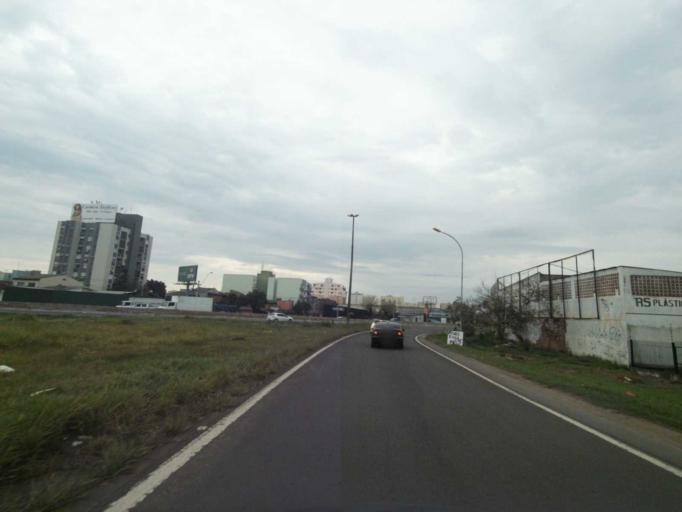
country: BR
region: Rio Grande do Sul
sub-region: Sao Leopoldo
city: Sao Leopoldo
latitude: -29.7622
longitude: -51.1533
